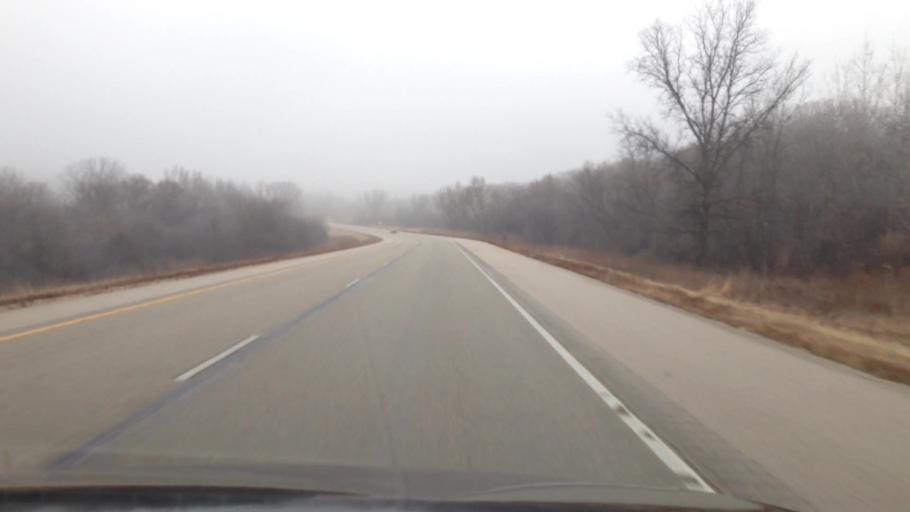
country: US
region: Wisconsin
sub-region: Walworth County
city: East Troy
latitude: 42.7212
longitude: -88.4663
